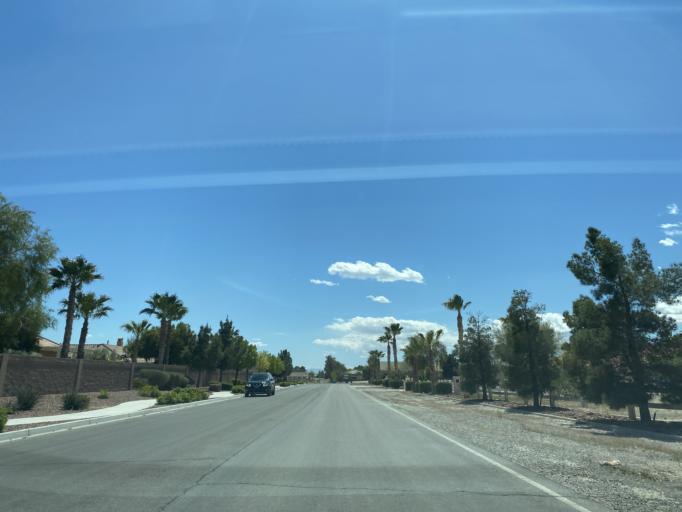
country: US
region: Nevada
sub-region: Clark County
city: North Las Vegas
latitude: 36.3122
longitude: -115.2311
